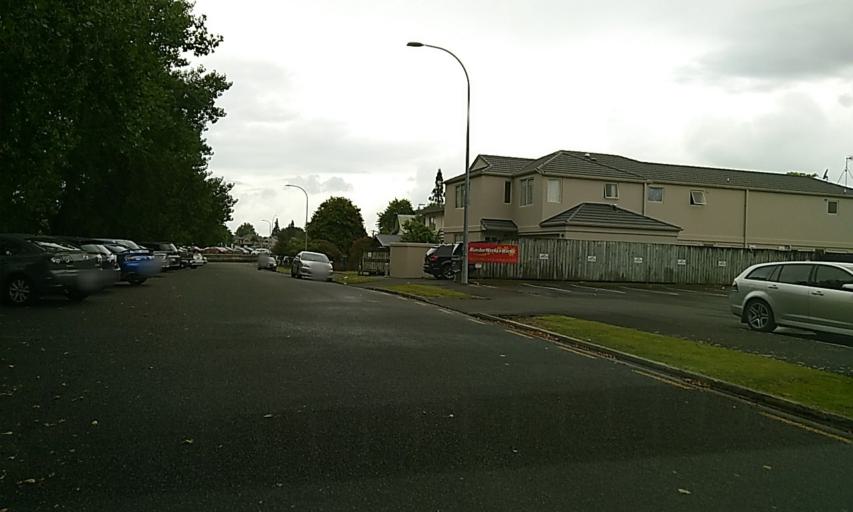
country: NZ
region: Waikato
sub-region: Hamilton City
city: Hamilton
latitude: -37.7845
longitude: 175.2688
